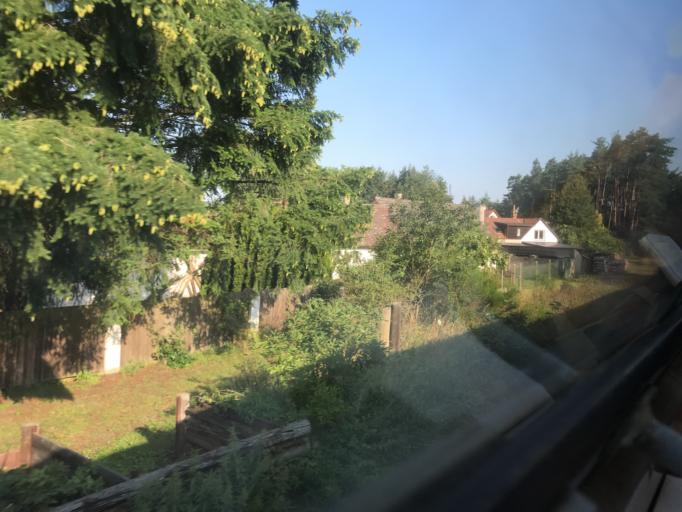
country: CZ
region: Jihocesky
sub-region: Okres Tabor
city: Veseli nad Luznici
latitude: 49.1533
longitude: 14.7255
